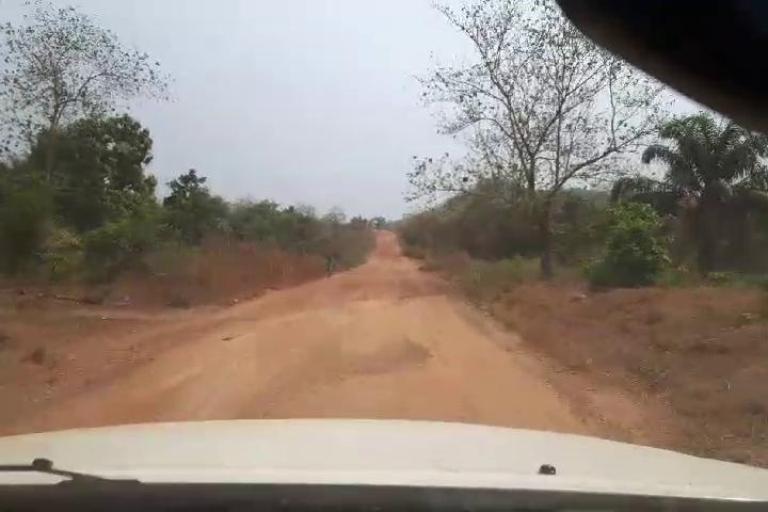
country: SL
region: Northern Province
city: Bumbuna
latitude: 9.0294
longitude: -11.7629
